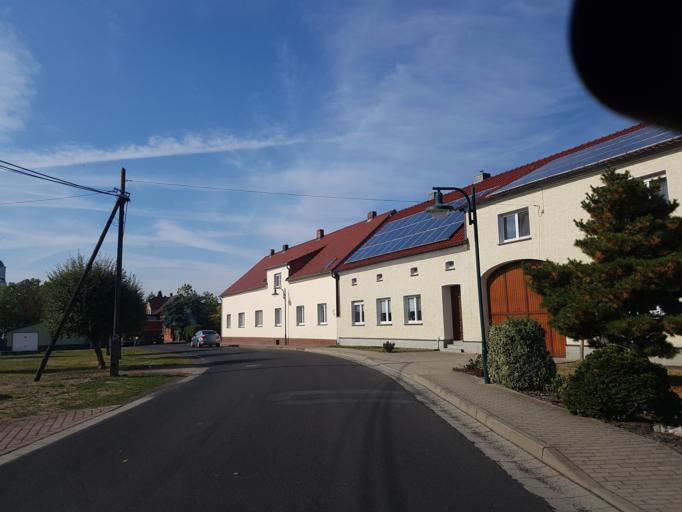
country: DE
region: Brandenburg
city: Hohenbucko
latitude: 51.6981
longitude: 13.4740
